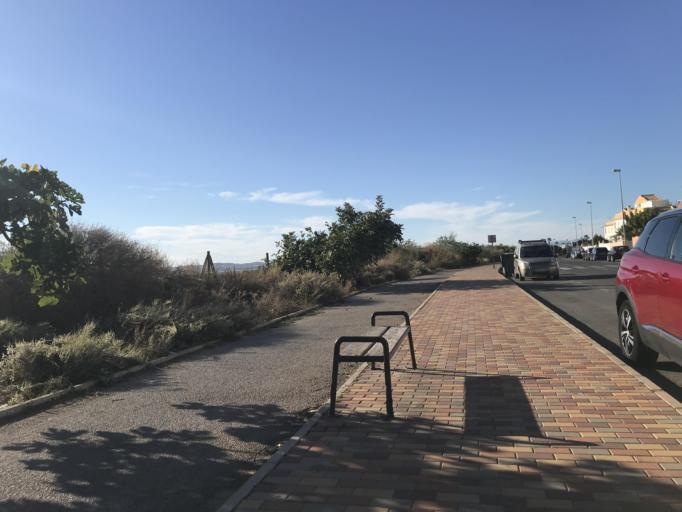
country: ES
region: Valencia
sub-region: Provincia de Alicante
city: Torrevieja
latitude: 37.9808
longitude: -0.6947
